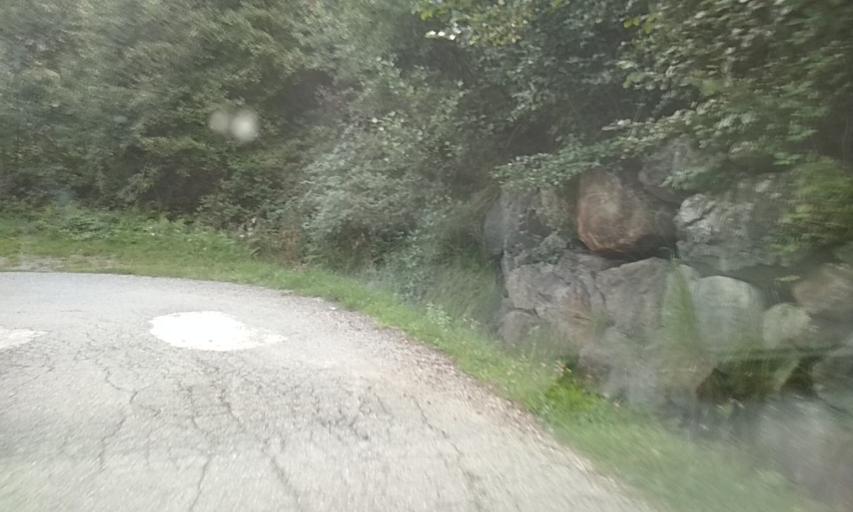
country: IT
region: Piedmont
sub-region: Provincia di Torino
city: Noasca
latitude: 45.4581
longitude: 7.3043
